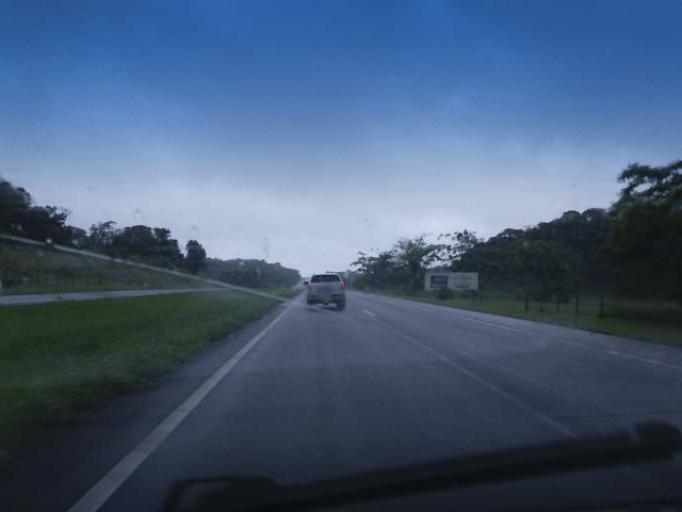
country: BR
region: Sao Paulo
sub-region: Registro
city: Registro
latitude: -24.5529
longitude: -47.8645
